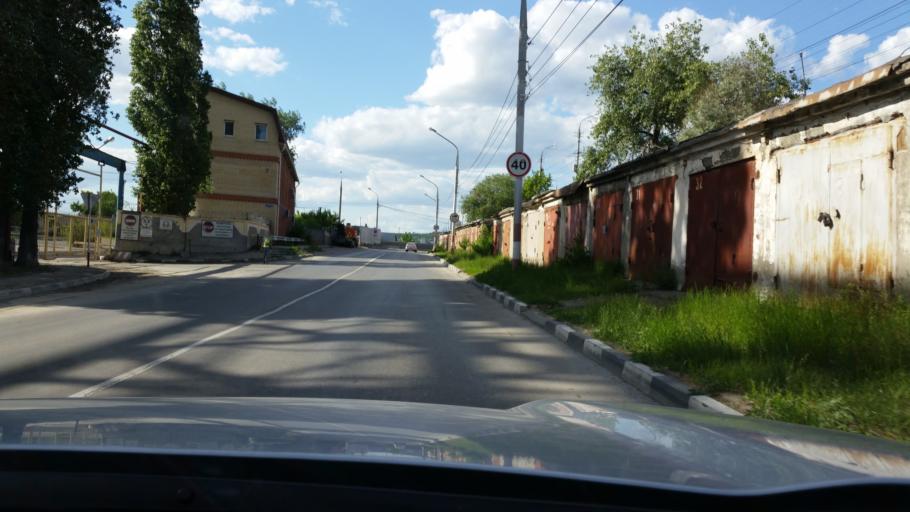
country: RU
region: Saratov
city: Engel's
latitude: 51.5046
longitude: 46.0784
